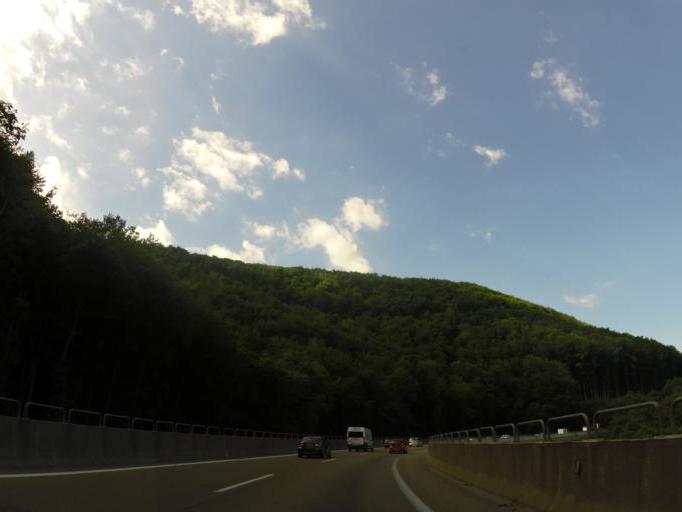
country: DE
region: Baden-Wuerttemberg
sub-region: Regierungsbezirk Stuttgart
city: Muhlhausen
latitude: 48.5673
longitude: 9.6464
